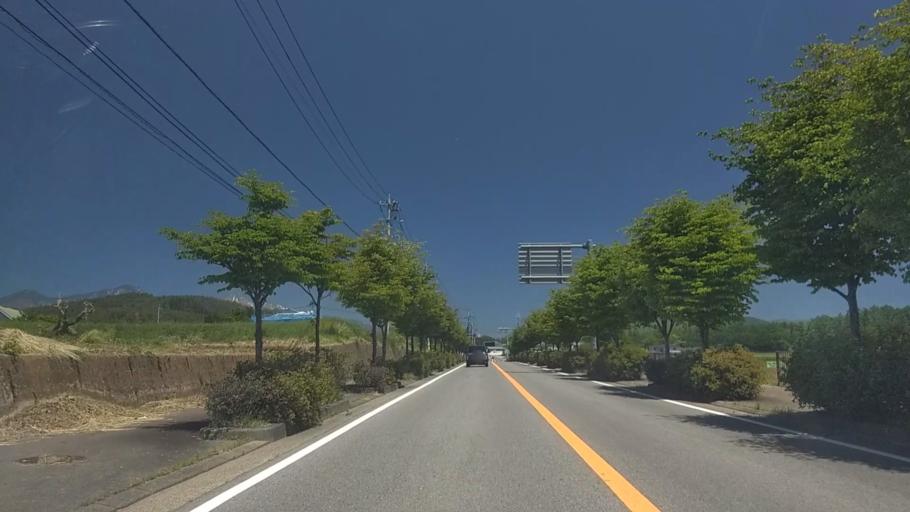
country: JP
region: Yamanashi
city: Nirasaki
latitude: 35.8418
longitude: 138.4332
